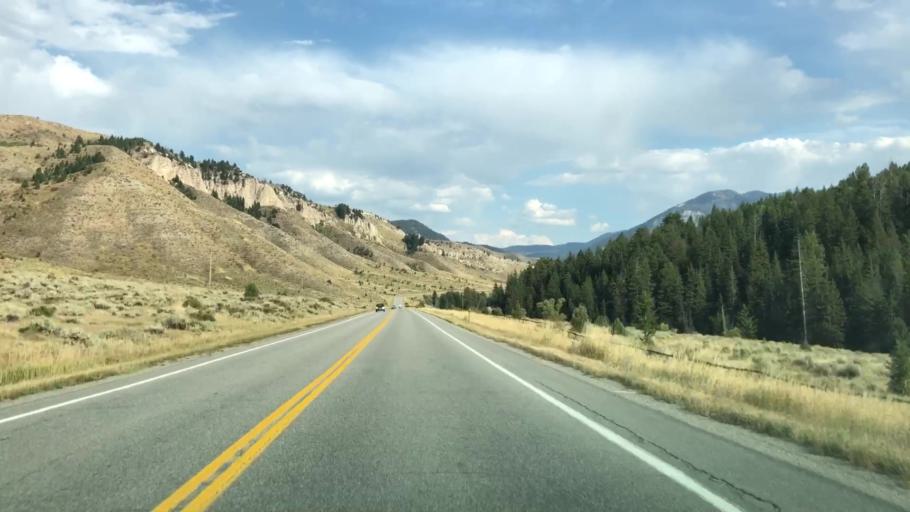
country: US
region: Wyoming
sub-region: Teton County
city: Hoback
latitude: 43.3170
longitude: -110.6974
